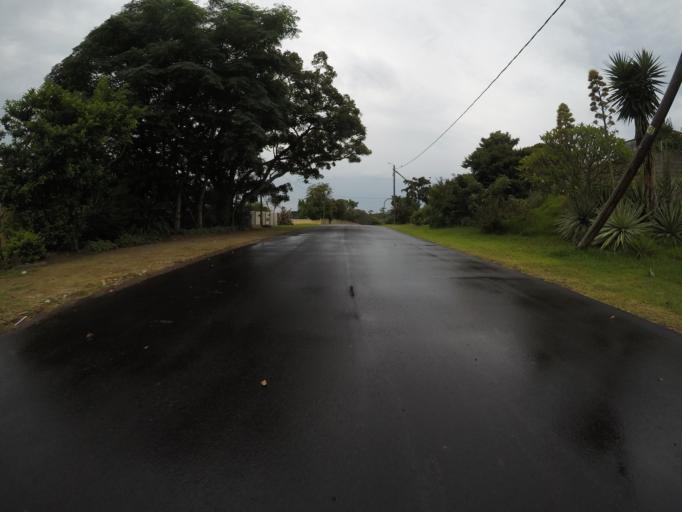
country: ZA
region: Eastern Cape
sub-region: Buffalo City Metropolitan Municipality
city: East London
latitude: -32.9631
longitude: 27.8453
